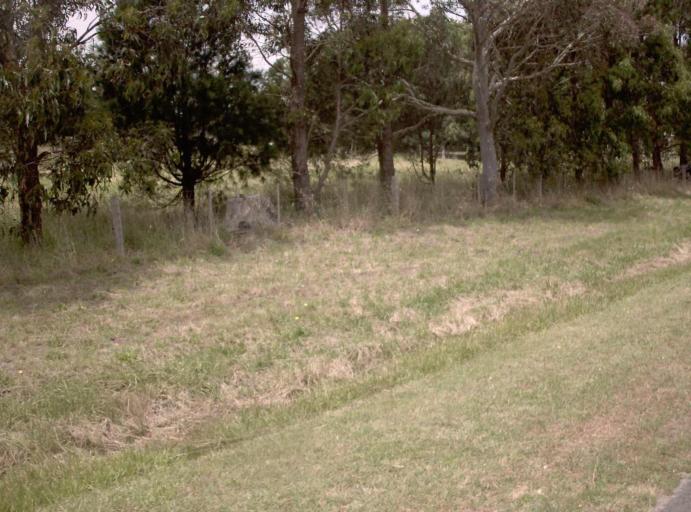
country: AU
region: Victoria
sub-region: Latrobe
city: Traralgon
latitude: -38.4973
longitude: 146.7119
